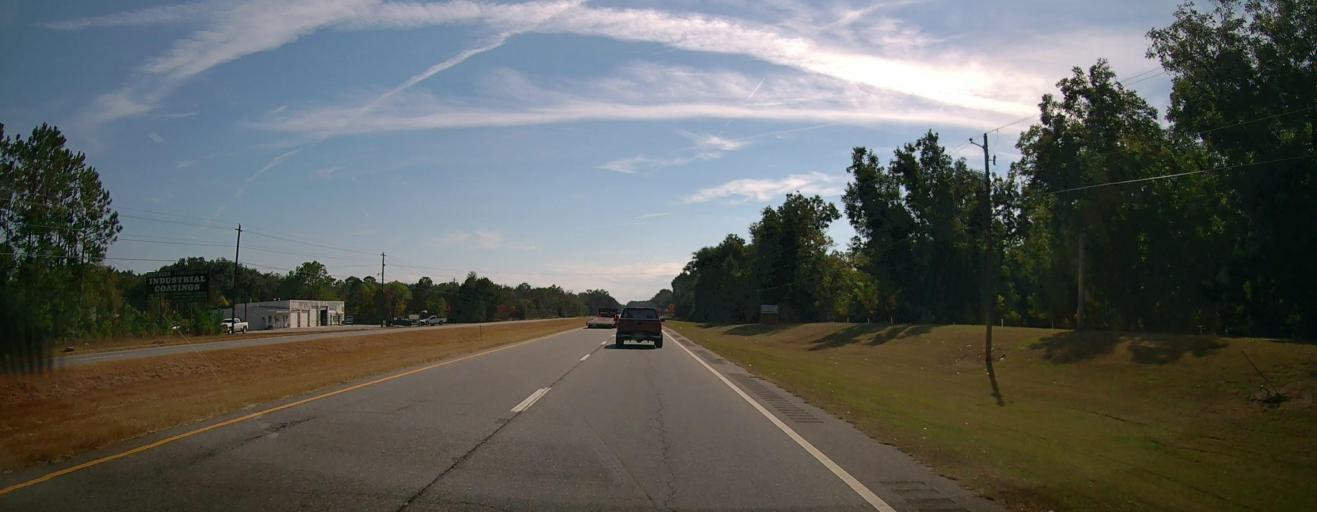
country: US
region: Georgia
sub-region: Dougherty County
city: Putney
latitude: 31.4807
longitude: -84.1171
